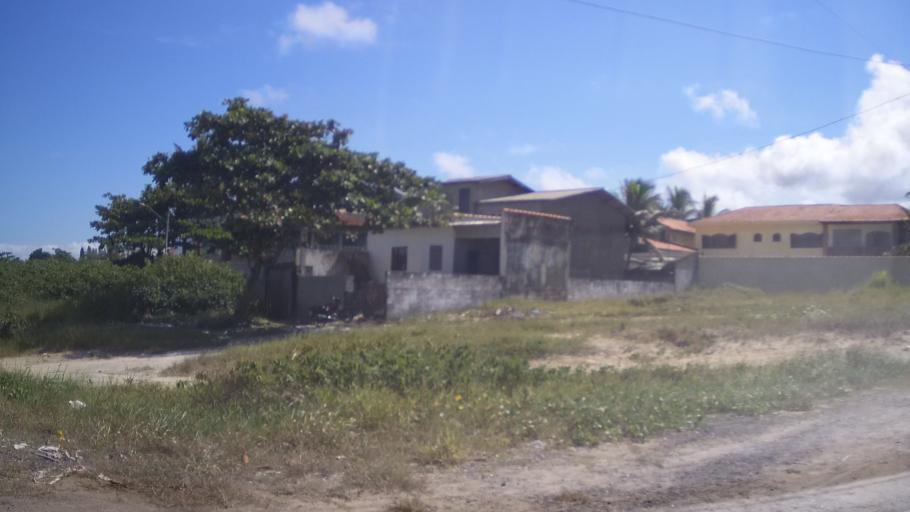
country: BR
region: Sao Paulo
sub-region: Itanhaem
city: Itanhaem
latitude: -24.1524
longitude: -46.7262
